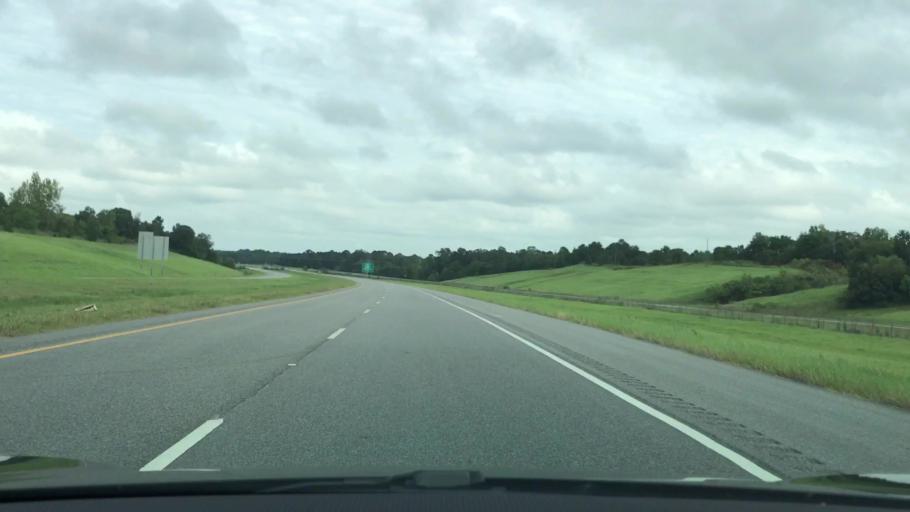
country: US
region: Alabama
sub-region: Montgomery County
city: Pike Road
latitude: 32.3486
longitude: -86.0650
